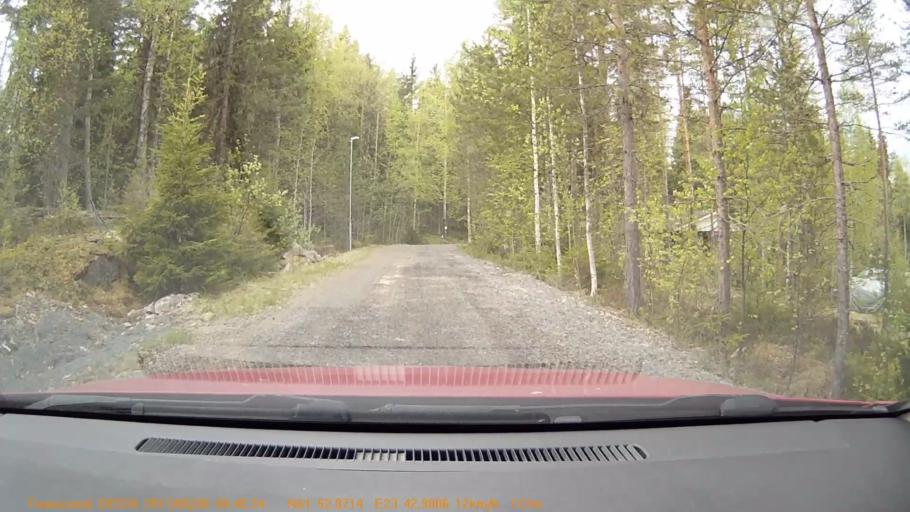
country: FI
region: Pirkanmaa
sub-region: Tampere
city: Kuru
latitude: 61.8812
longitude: 23.7151
